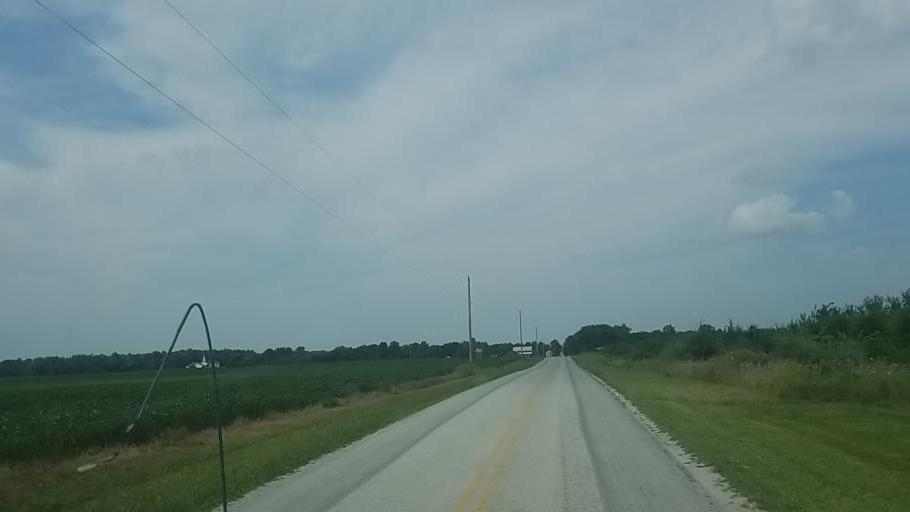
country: US
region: Ohio
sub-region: Hardin County
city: Forest
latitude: 40.7750
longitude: -83.5764
